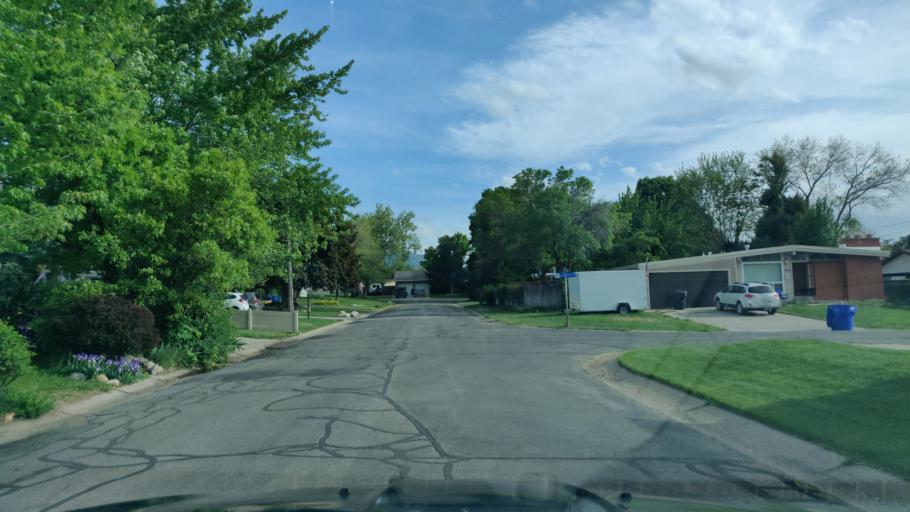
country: US
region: Utah
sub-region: Salt Lake County
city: Cottonwood Heights
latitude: 40.6187
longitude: -111.8134
